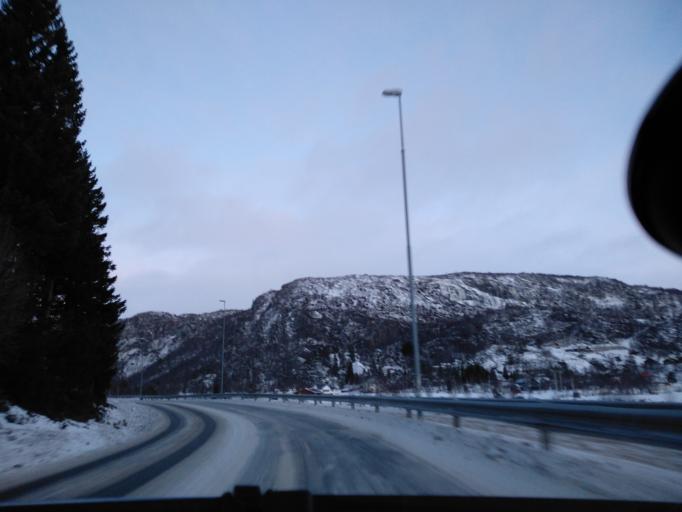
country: NO
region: Vest-Agder
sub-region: Sirdal
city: Tonstad
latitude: 58.9226
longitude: 6.9042
